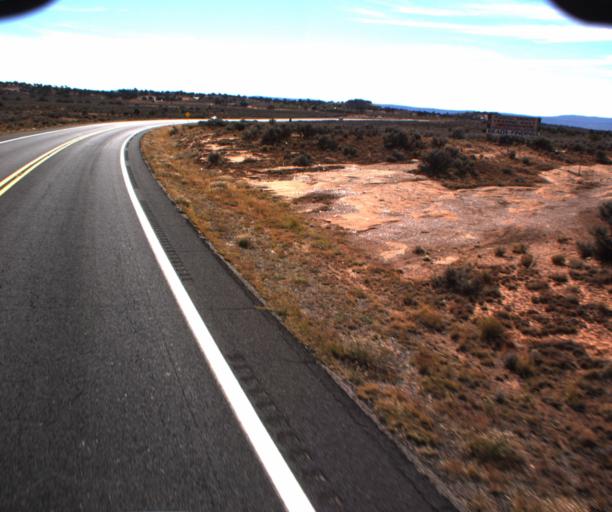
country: US
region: Arizona
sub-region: Coconino County
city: Kaibito
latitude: 36.5517
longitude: -110.7032
